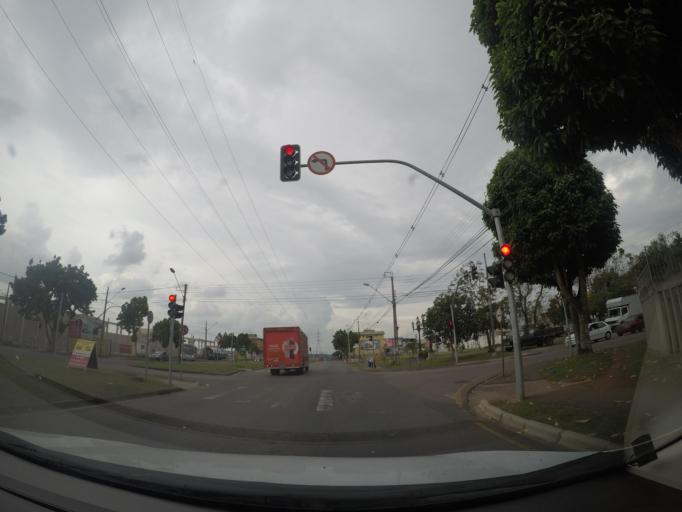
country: BR
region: Parana
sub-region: Sao Jose Dos Pinhais
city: Sao Jose dos Pinhais
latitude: -25.5475
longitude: -49.2610
